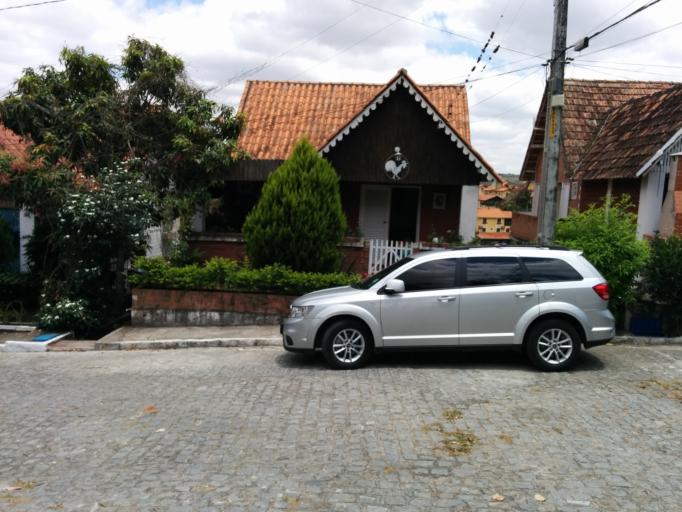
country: BR
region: Pernambuco
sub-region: Gravata
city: Gravata
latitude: -8.1934
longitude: -35.5606
